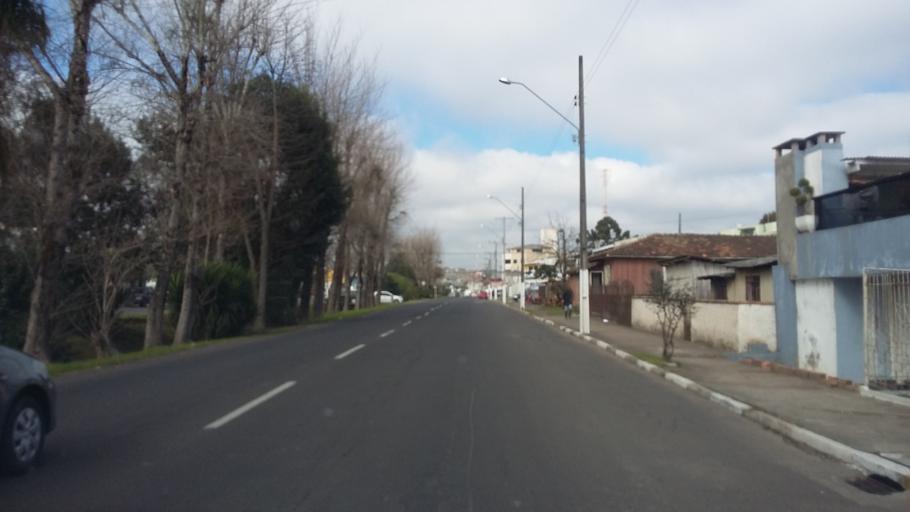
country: BR
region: Santa Catarina
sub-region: Lages
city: Lages
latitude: -27.8200
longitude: -50.3390
